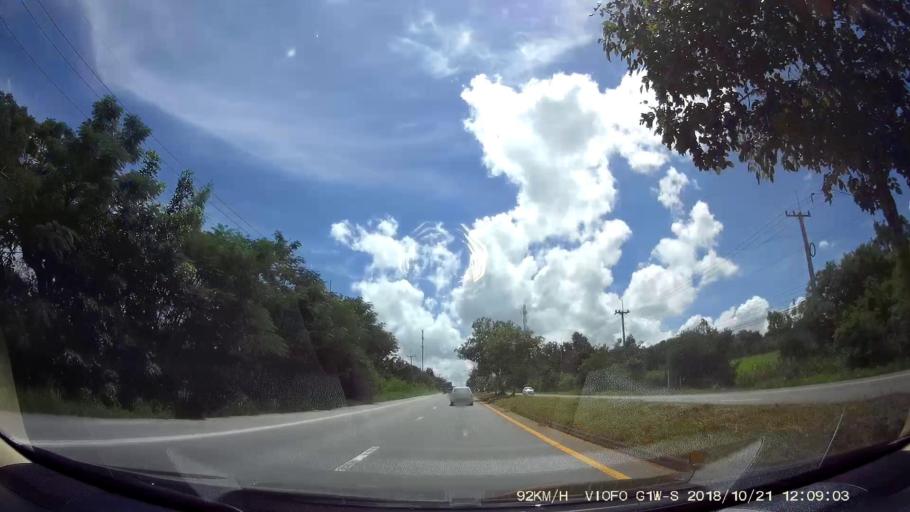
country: TH
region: Chaiyaphum
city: Chatturat
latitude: 15.4254
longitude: 101.8318
